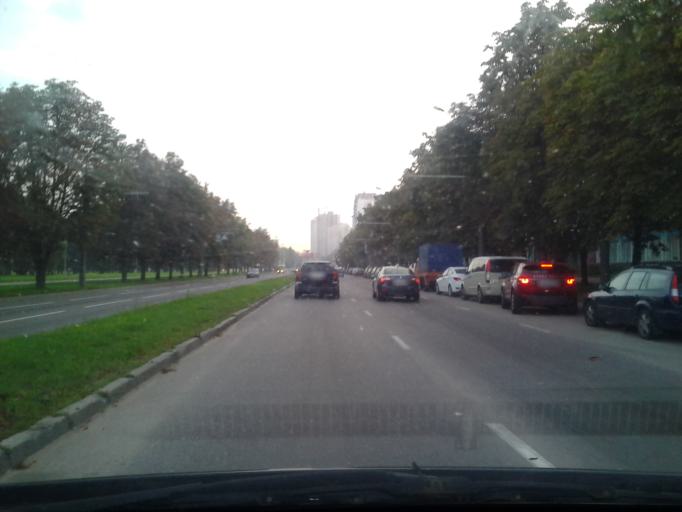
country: BY
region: Minsk
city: Minsk
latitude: 53.9282
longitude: 27.5738
